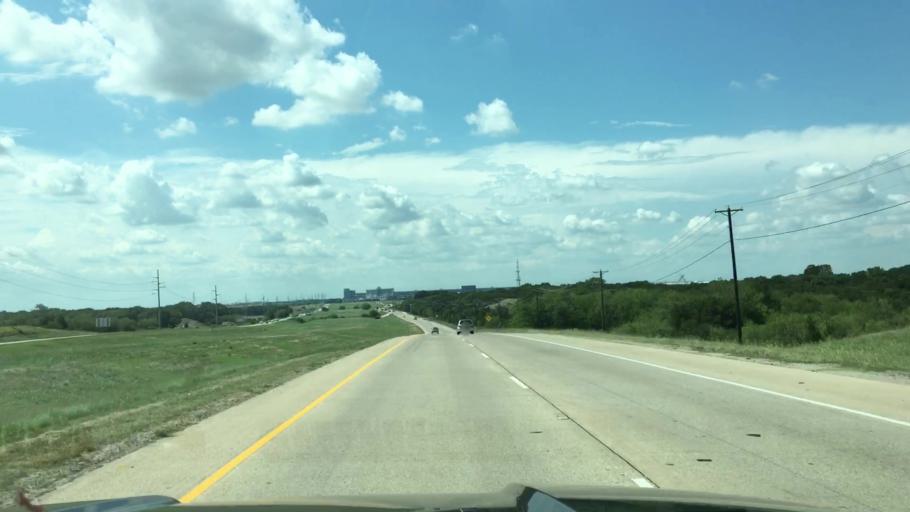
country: US
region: Texas
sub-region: Denton County
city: Roanoke
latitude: 33.0180
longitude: -97.2404
